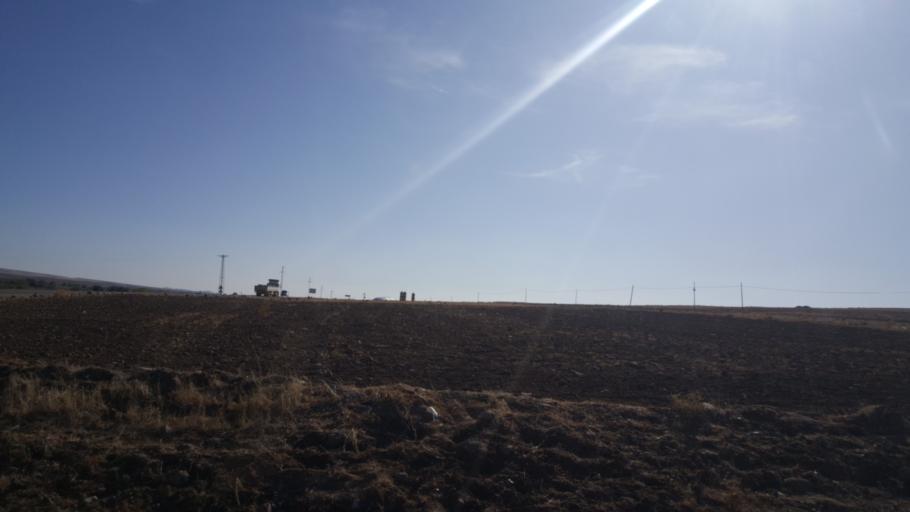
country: TR
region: Ankara
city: Altpinar
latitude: 39.2401
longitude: 32.7429
